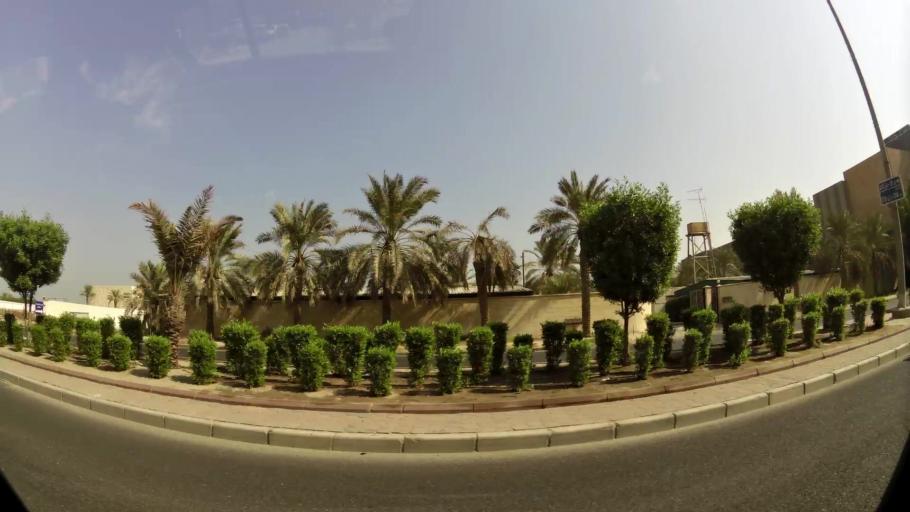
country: KW
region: Al Ahmadi
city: Al Mahbulah
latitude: 29.1545
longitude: 48.1243
